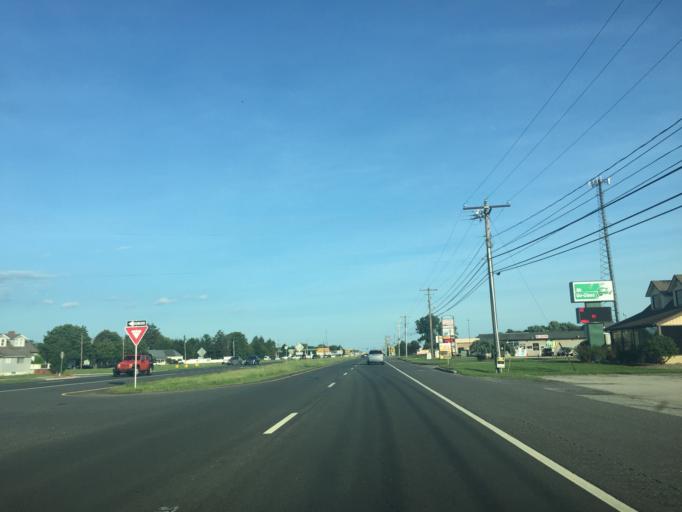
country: US
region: Delaware
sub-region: Kent County
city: Cheswold
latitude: 39.2052
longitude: -75.5632
